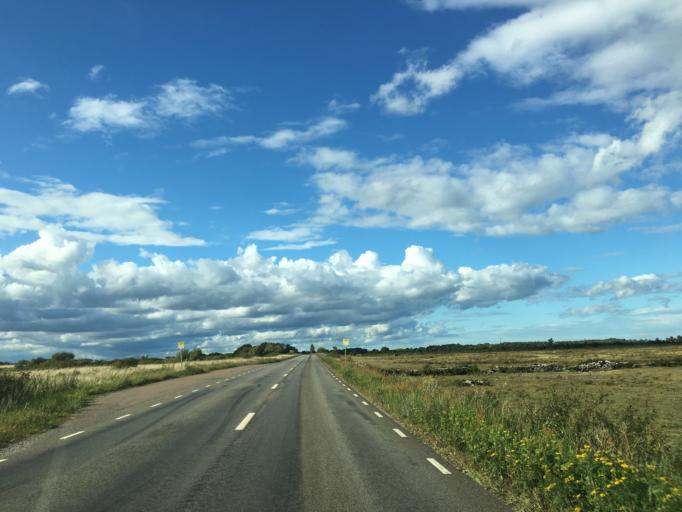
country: SE
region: Kalmar
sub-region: Morbylanga Kommun
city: Moerbylanga
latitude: 56.4895
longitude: 16.4262
